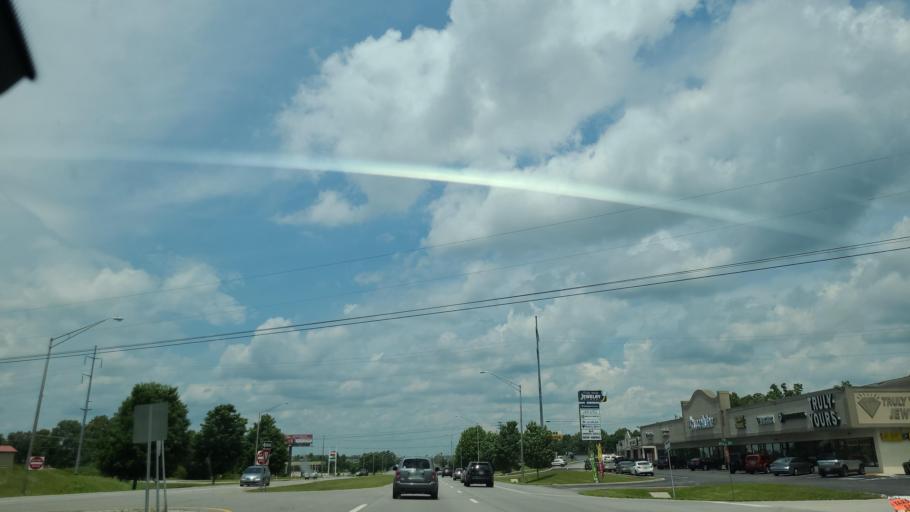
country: US
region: Tennessee
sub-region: Cumberland County
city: Crossville
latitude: 35.9710
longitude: -85.0380
